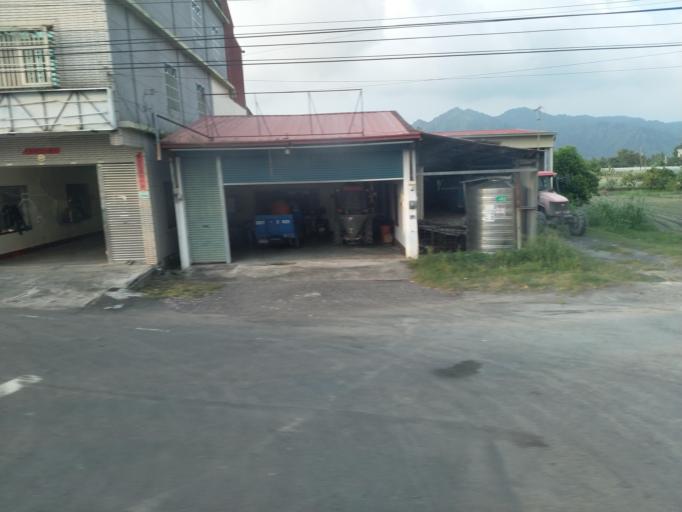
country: TW
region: Taiwan
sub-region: Pingtung
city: Pingtung
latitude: 22.8866
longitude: 120.5258
